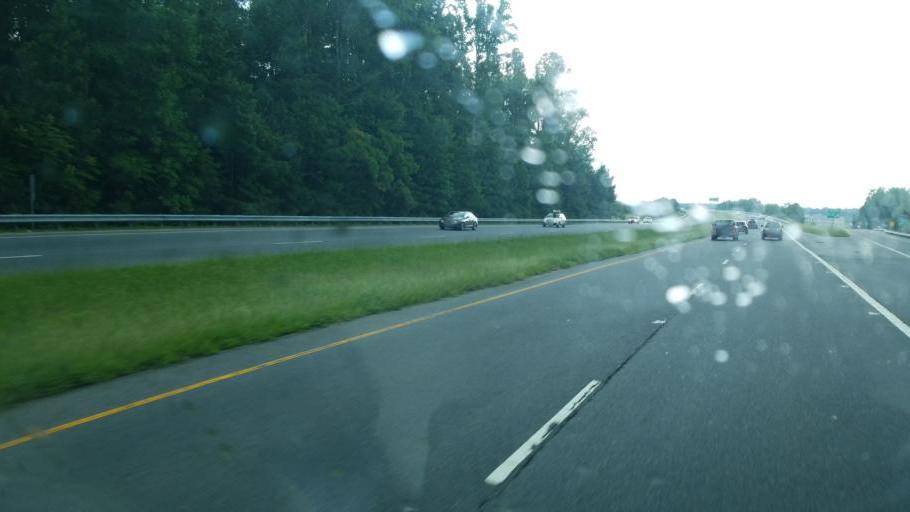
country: US
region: North Carolina
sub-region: Currituck County
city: Moyock
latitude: 36.6628
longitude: -76.2306
